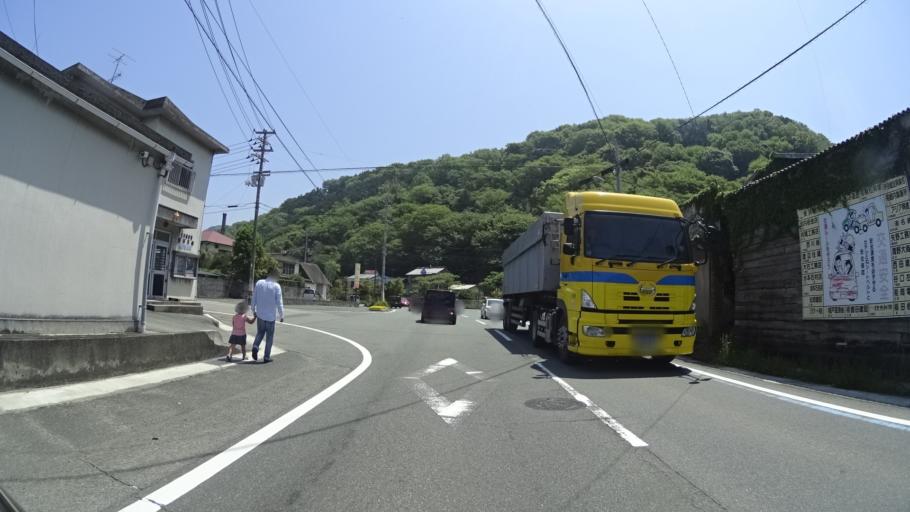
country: JP
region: Ehime
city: Ozu
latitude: 33.6149
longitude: 132.4843
